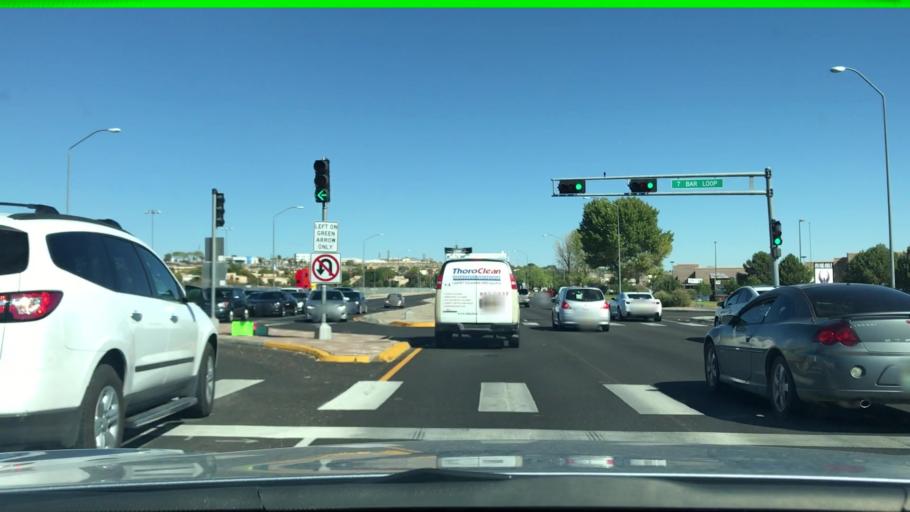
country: US
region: New Mexico
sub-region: Sandoval County
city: Rio Rancho
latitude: 35.2011
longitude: -106.6603
